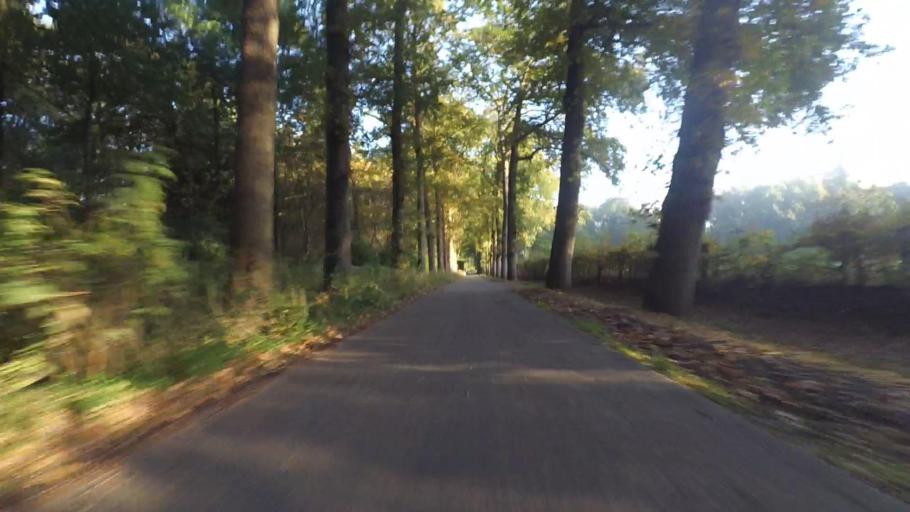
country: NL
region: Utrecht
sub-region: Gemeente De Bilt
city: De Bilt
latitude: 52.1629
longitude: 5.2014
